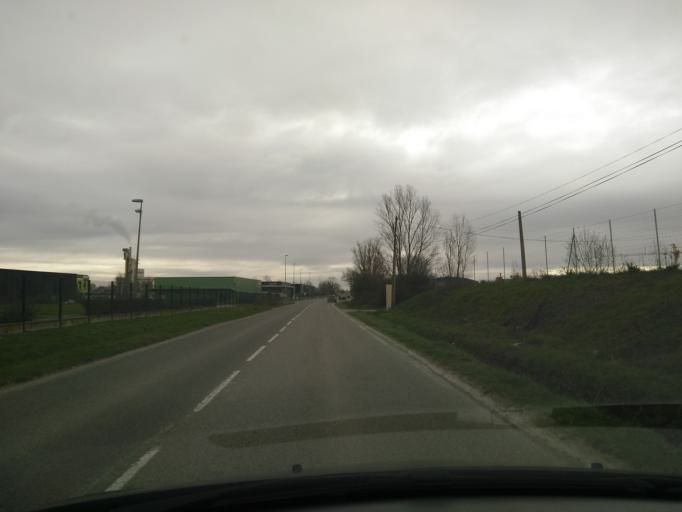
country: FR
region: Midi-Pyrenees
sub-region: Departement de la Haute-Garonne
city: Cugnaux
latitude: 43.5318
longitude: 1.3678
